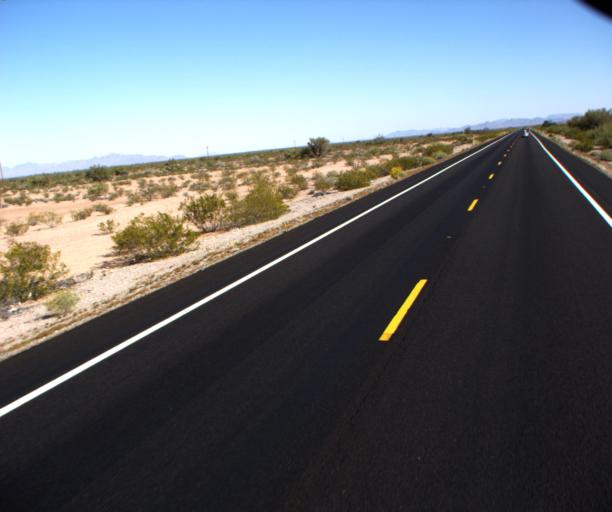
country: US
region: Arizona
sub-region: La Paz County
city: Quartzsite
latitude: 33.2804
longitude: -114.2315
